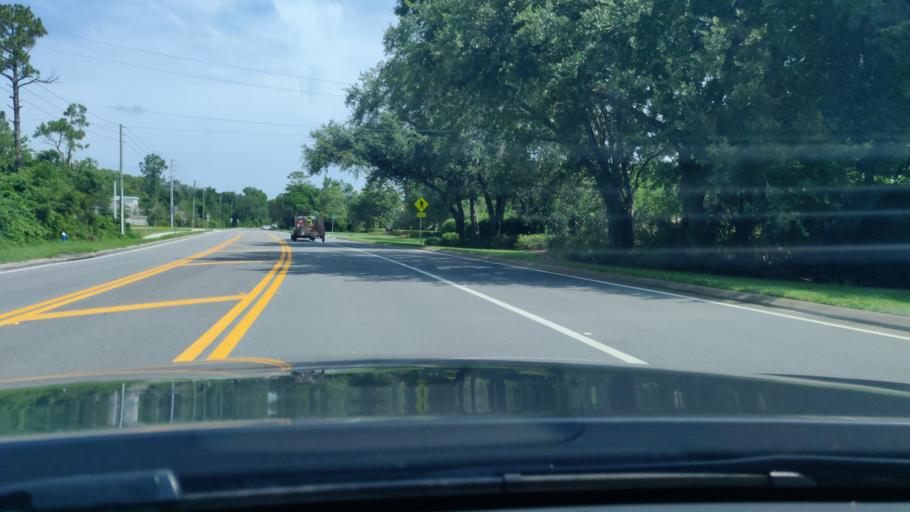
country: US
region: Florida
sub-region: Flagler County
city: Palm Coast
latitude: 29.5454
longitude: -81.1759
